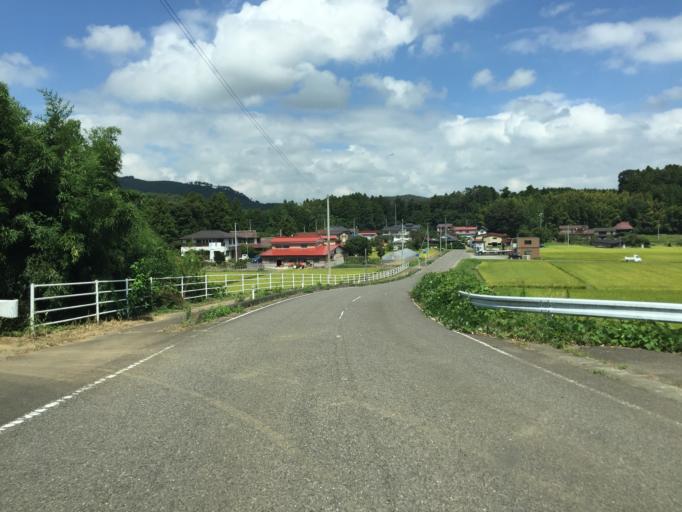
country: JP
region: Fukushima
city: Motomiya
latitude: 37.5506
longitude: 140.3764
